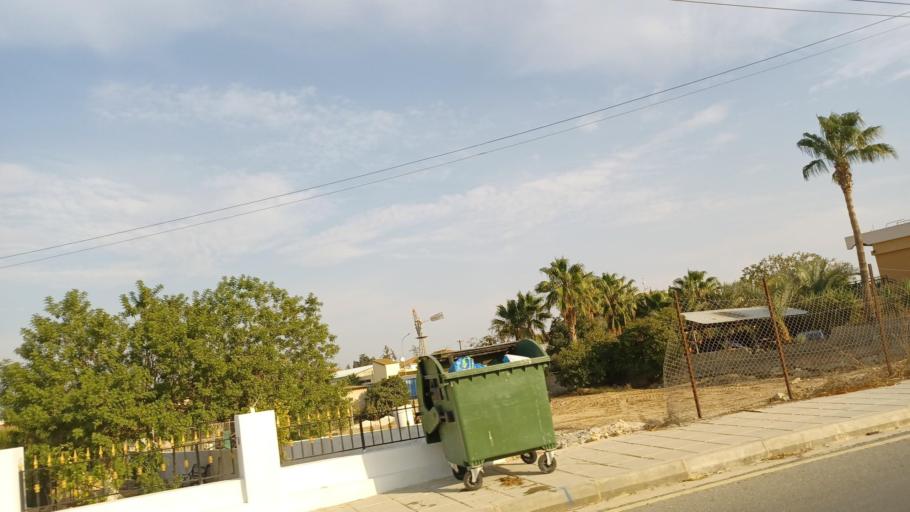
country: CY
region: Ammochostos
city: Acheritou
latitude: 35.0799
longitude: 33.8732
